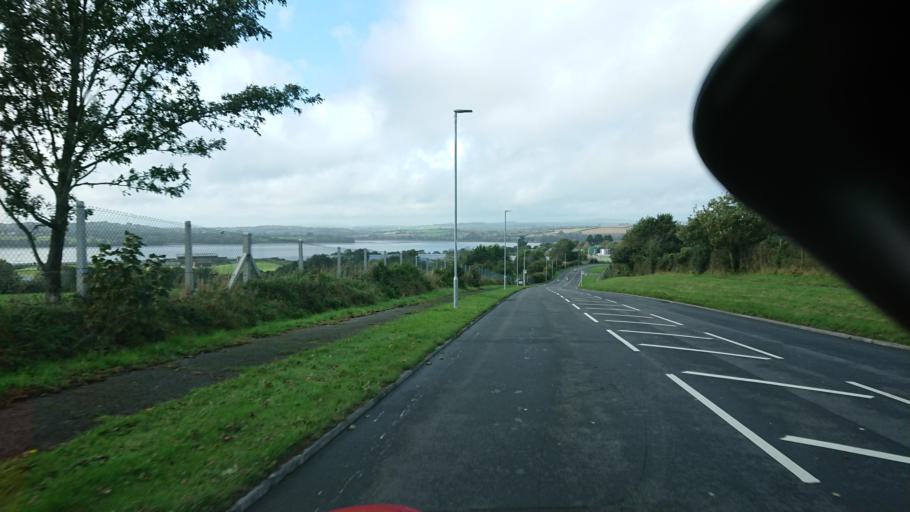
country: GB
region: England
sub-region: Cornwall
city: Saltash
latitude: 50.4152
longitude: -4.1852
